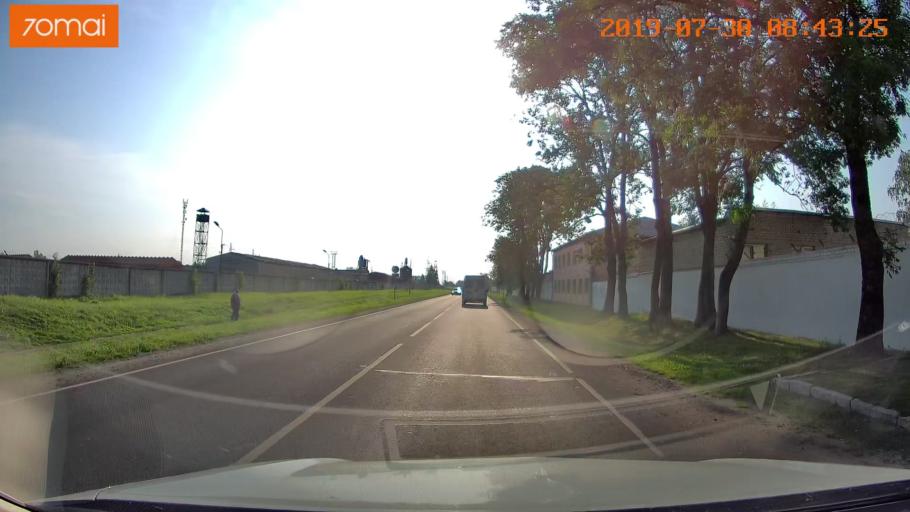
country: RU
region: Kaliningrad
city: Chernyakhovsk
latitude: 54.6270
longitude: 21.8407
